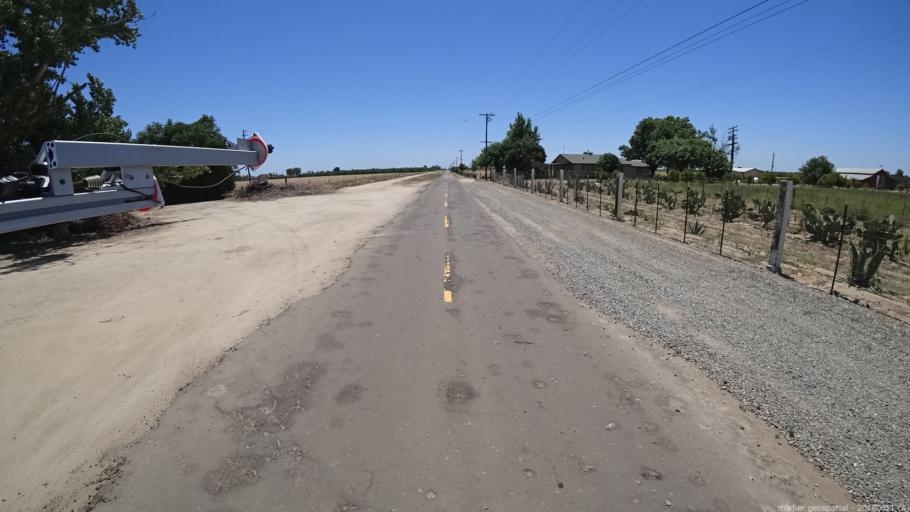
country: US
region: California
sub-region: Madera County
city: Fairmead
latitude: 37.0152
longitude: -120.1932
